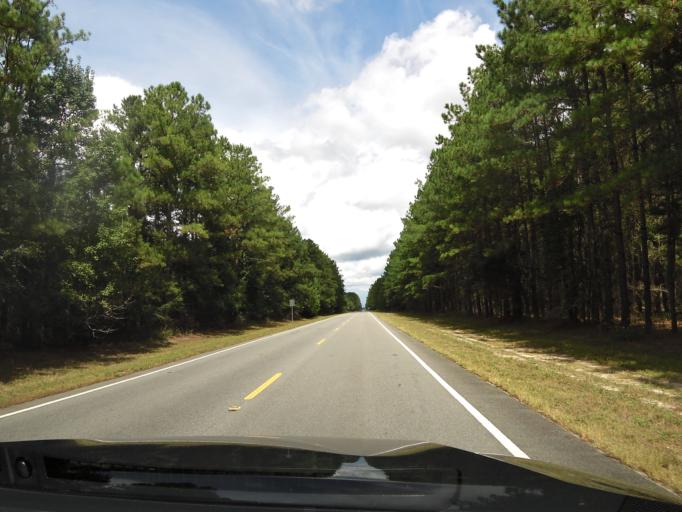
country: US
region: Georgia
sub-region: Brantley County
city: Nahunta
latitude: 31.0611
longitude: -82.0147
